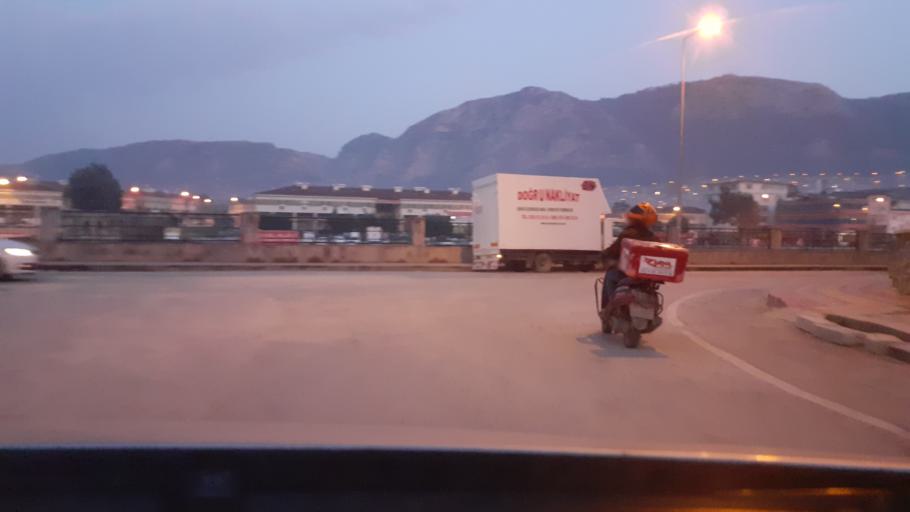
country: TR
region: Hatay
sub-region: Antakya Ilcesi
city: Antakya
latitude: 36.2126
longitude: 36.1612
